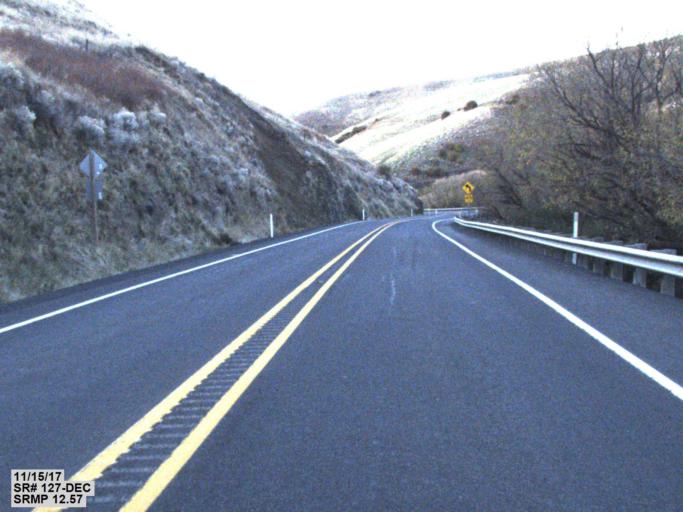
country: US
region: Washington
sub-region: Garfield County
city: Pomeroy
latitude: 46.6607
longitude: -117.8006
